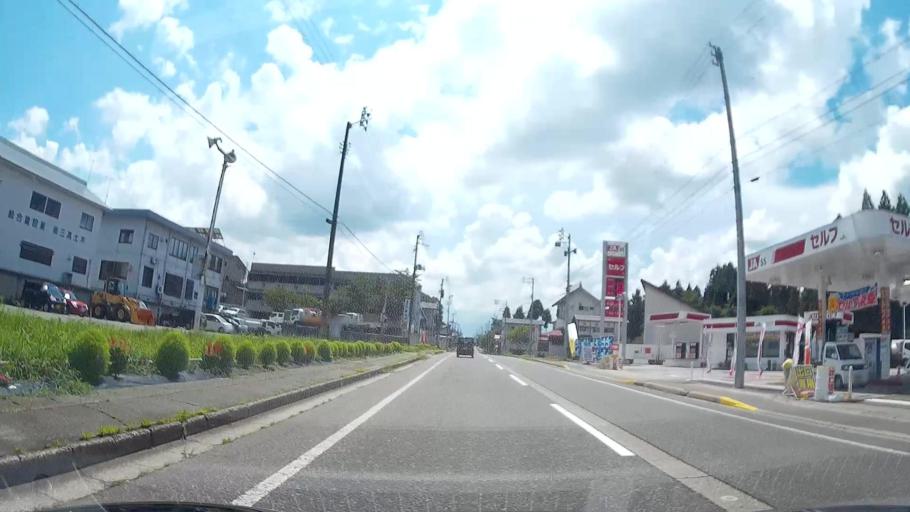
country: JP
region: Niigata
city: Tokamachi
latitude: 37.0606
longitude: 138.7071
